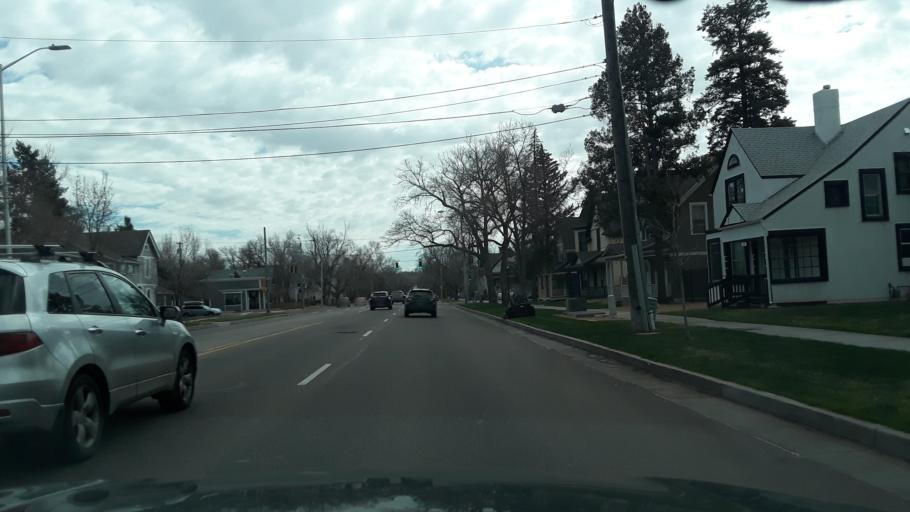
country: US
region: Colorado
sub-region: El Paso County
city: Colorado Springs
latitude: 38.8505
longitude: -104.8202
